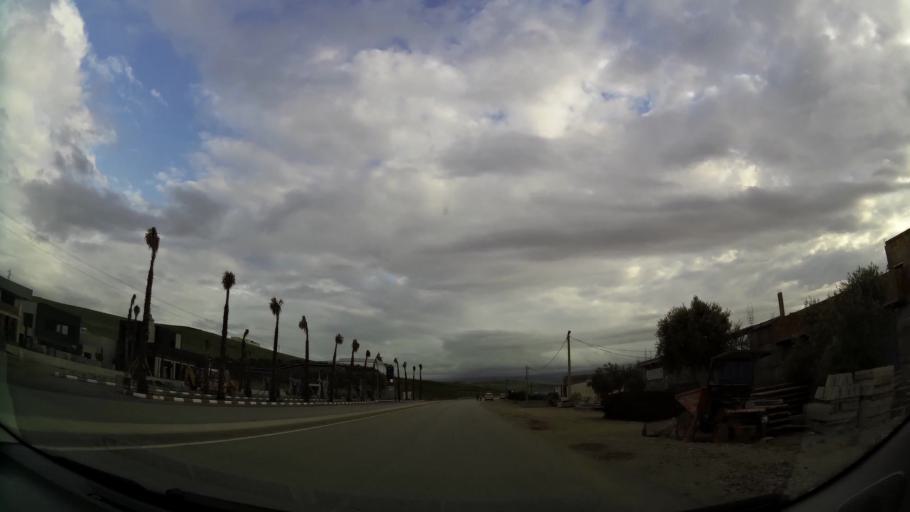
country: MA
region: Taza-Al Hoceima-Taounate
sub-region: Taza
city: Taza
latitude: 34.2674
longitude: -3.9571
